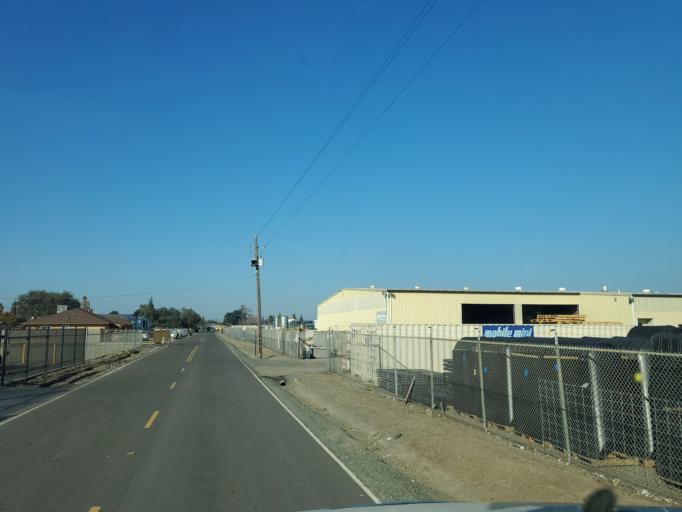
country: US
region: California
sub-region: San Joaquin County
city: August
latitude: 37.9784
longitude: -121.2531
